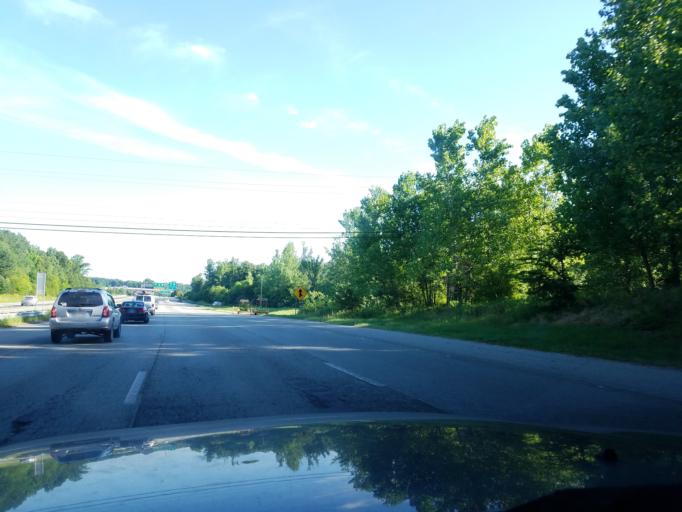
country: US
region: North Carolina
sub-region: Durham County
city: Durham
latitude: 36.0055
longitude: -78.8643
